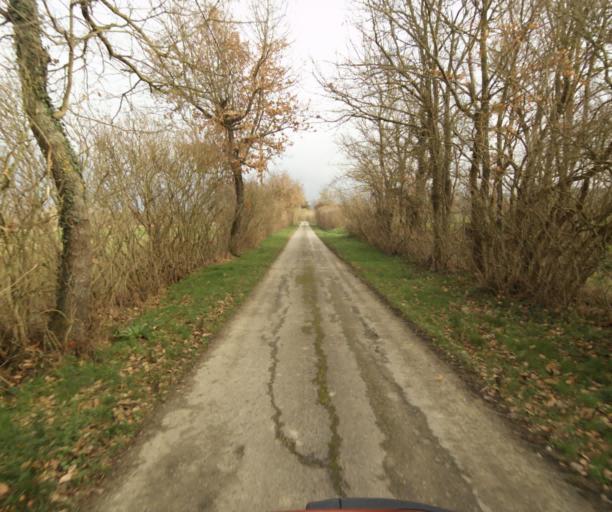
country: FR
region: Languedoc-Roussillon
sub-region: Departement de l'Aude
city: Belpech
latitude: 43.1895
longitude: 1.7316
